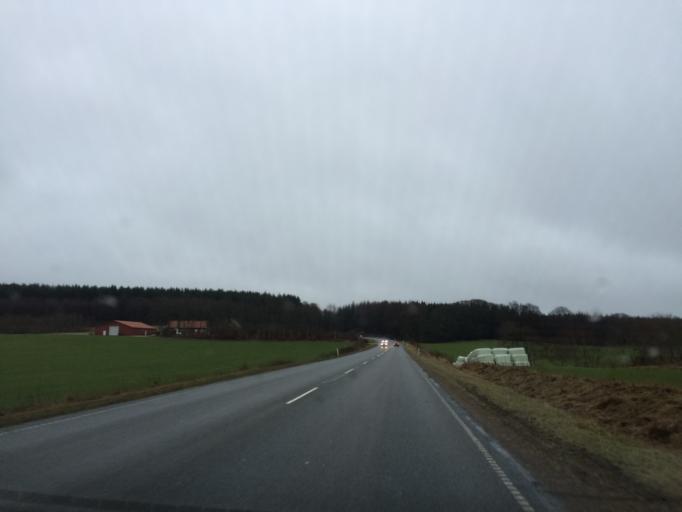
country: DK
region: North Denmark
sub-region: Mariagerfjord Kommune
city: Arden
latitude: 56.8060
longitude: 9.8176
